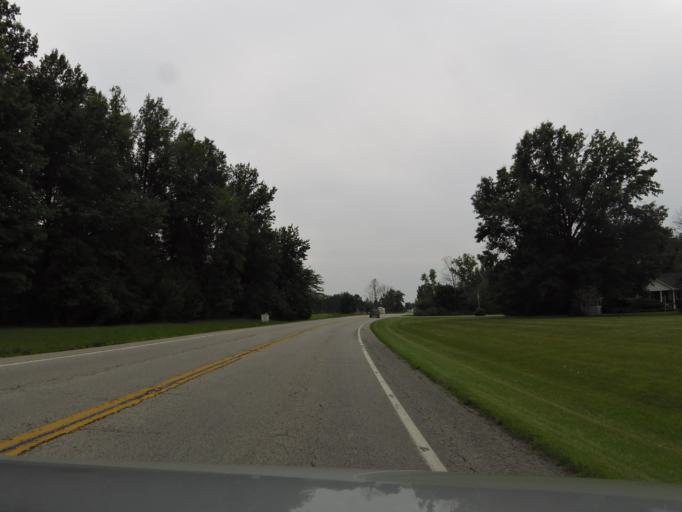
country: US
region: Ohio
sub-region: Brown County
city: Mount Orab
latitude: 39.0739
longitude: -83.9250
